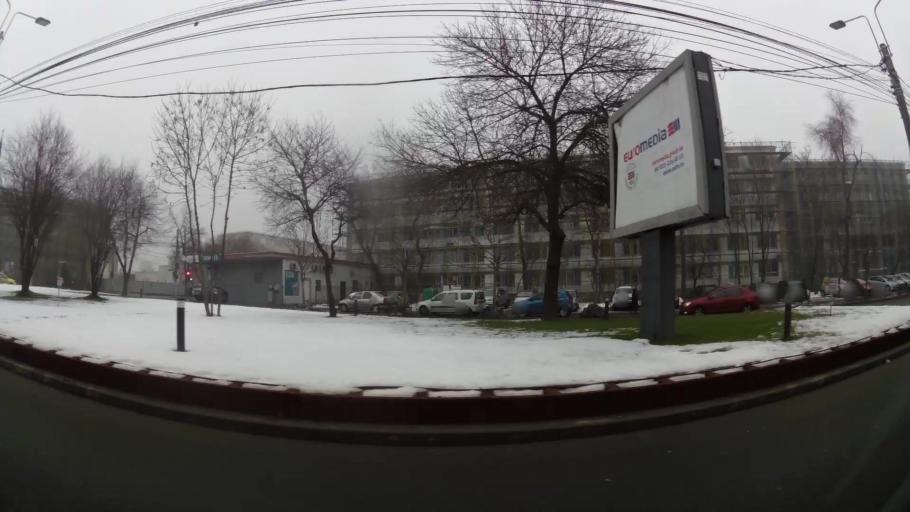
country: RO
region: Ilfov
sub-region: Comuna Chiajna
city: Rosu
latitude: 44.4629
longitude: 26.0410
